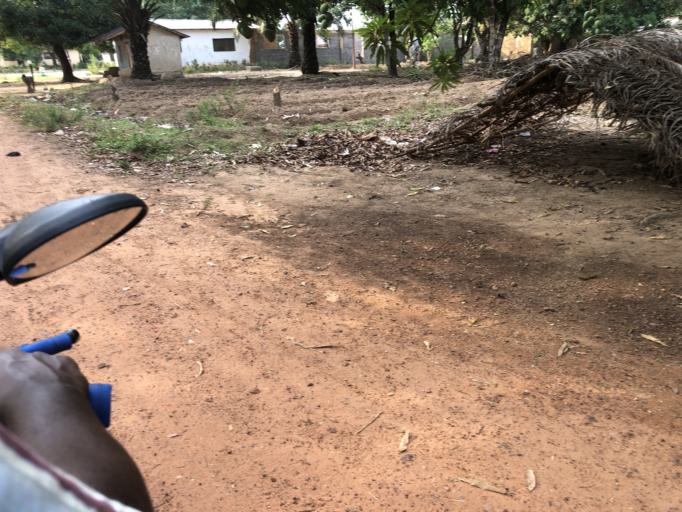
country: SL
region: Northern Province
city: Yonibana
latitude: 8.4616
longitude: -12.2042
